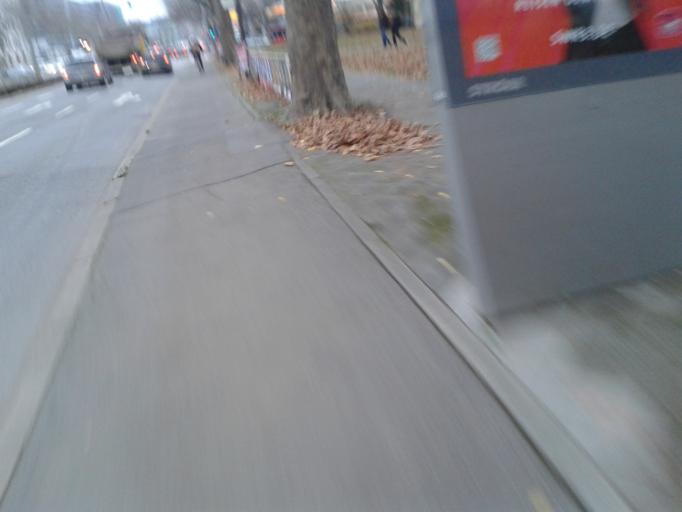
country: DE
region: Baden-Wuerttemberg
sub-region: Karlsruhe Region
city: Heidelberg
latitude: 49.4160
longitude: 8.6766
